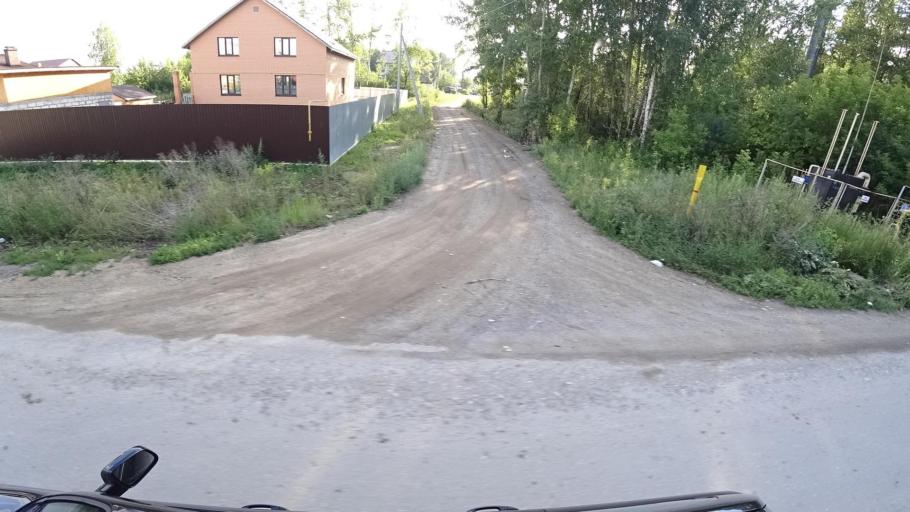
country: RU
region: Sverdlovsk
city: Obukhovskoye
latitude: 56.8475
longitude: 62.6543
